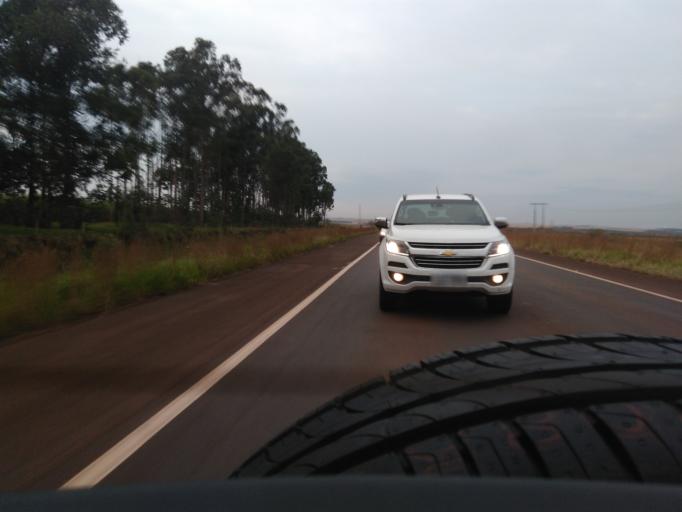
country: BR
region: Mato Grosso do Sul
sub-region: Dourados
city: Dourados
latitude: -22.3000
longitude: -55.0930
